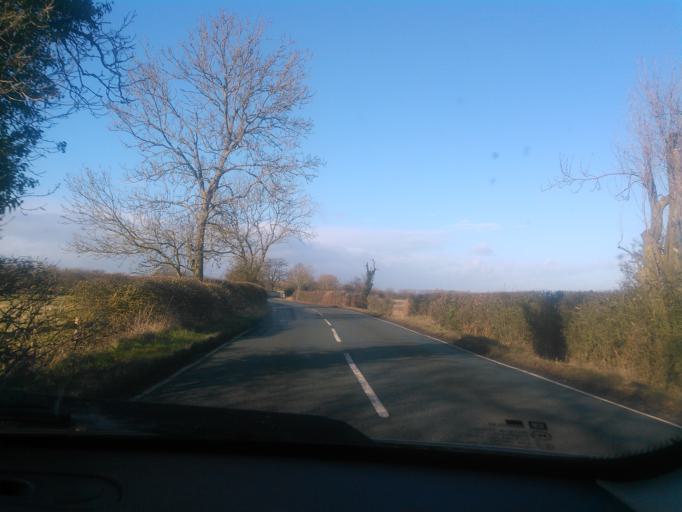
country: GB
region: England
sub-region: Telford and Wrekin
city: Eyton upon the Weald Moors
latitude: 52.7274
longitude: -2.5469
